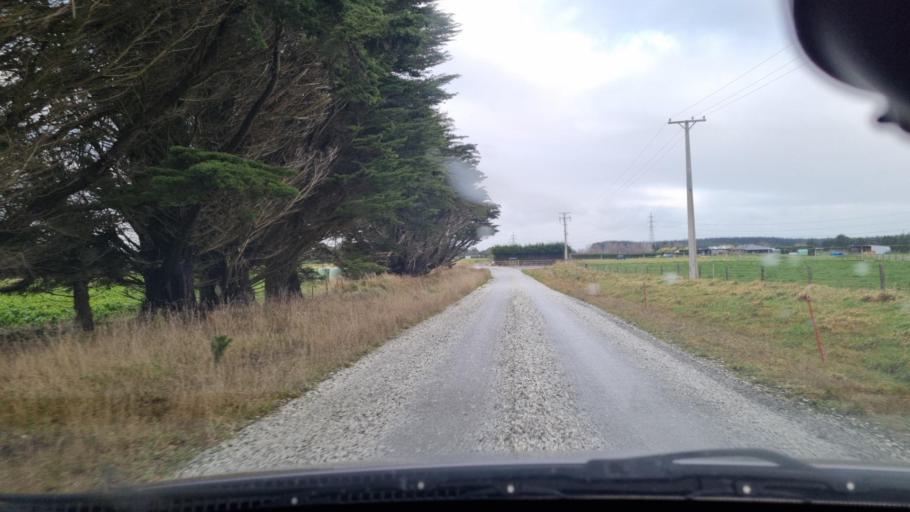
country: NZ
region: Southland
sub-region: Invercargill City
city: Invercargill
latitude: -46.4213
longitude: 168.4455
